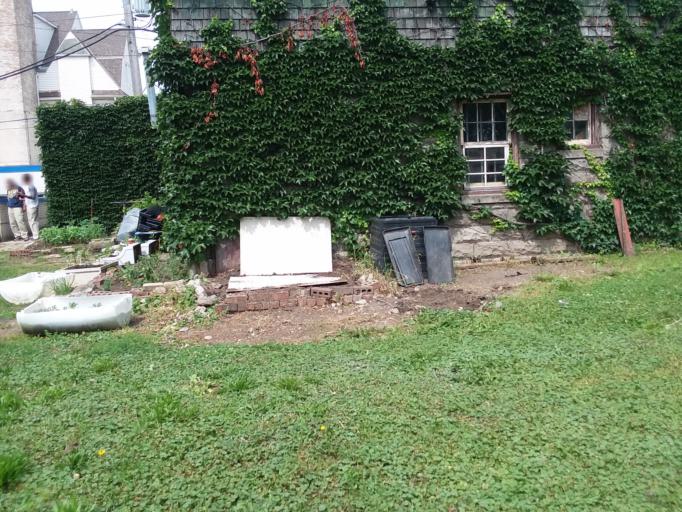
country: US
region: Wisconsin
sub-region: Milwaukee County
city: West Milwaukee
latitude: 43.0408
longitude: -87.9556
